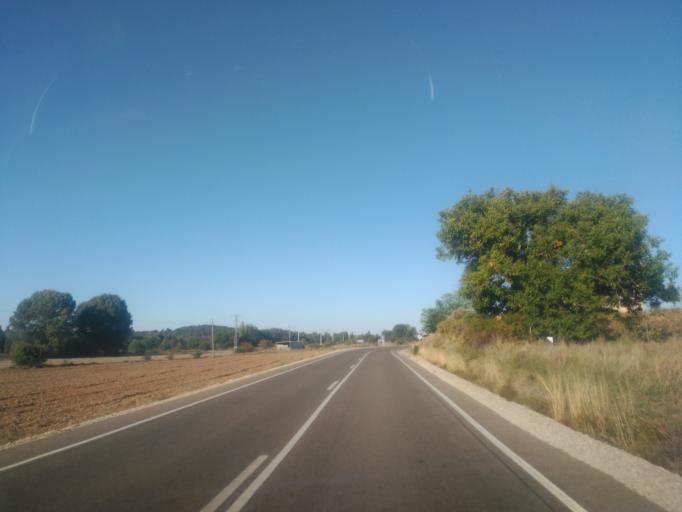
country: ES
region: Castille and Leon
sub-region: Provincia de Burgos
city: Zazuar
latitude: 41.6938
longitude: -3.5447
